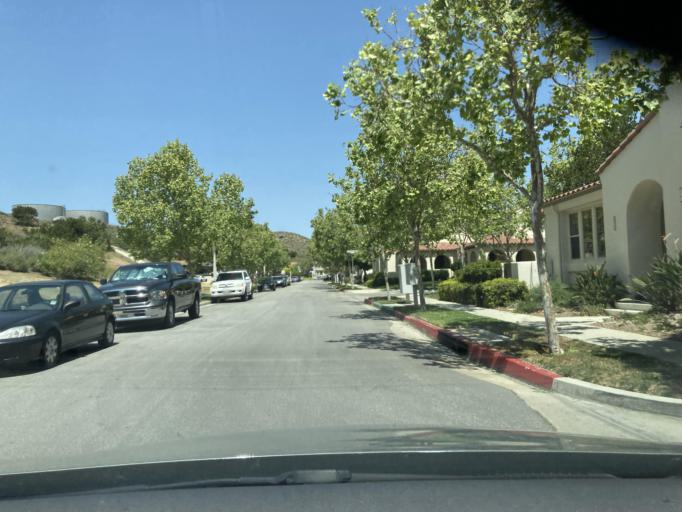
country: US
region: California
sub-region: Ventura County
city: Camarillo
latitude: 34.1671
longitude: -119.0358
